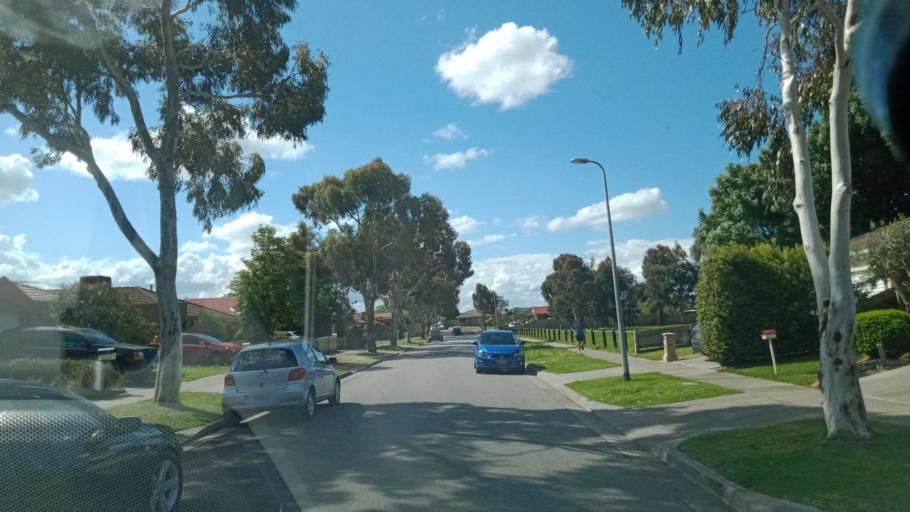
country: AU
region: Victoria
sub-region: Casey
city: Cranbourne West
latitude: -38.1002
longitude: 145.2613
